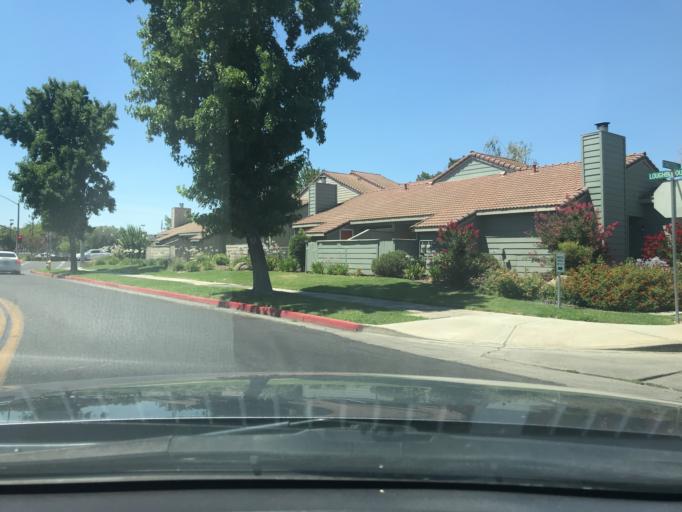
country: US
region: California
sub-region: Merced County
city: Merced
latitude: 37.3198
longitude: -120.4998
